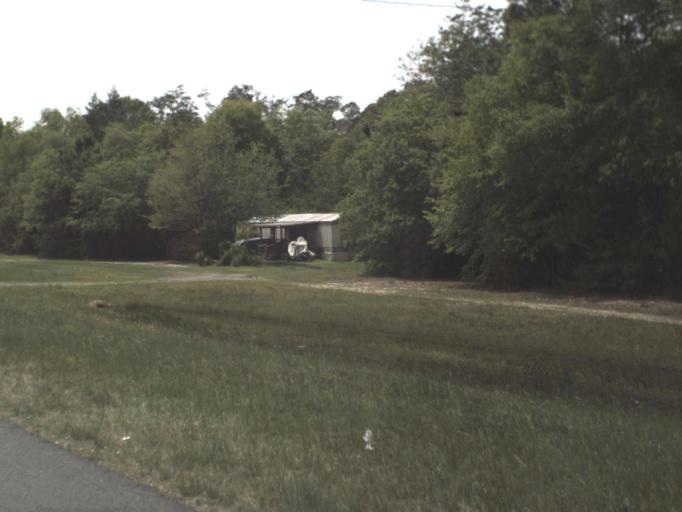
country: US
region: Florida
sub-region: Escambia County
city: Myrtle Grove
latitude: 30.4192
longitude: -87.3302
